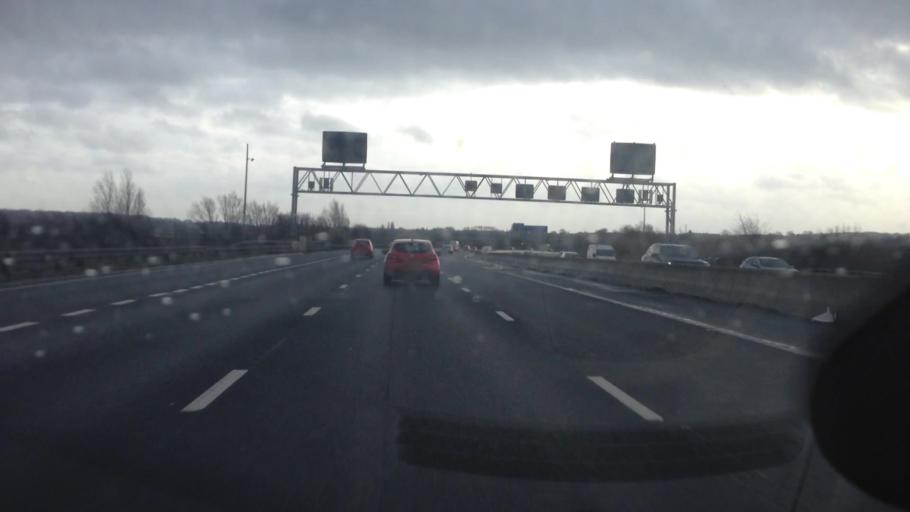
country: GB
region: England
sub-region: City and Borough of Wakefield
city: Crigglestone
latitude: 53.6589
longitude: -1.5310
